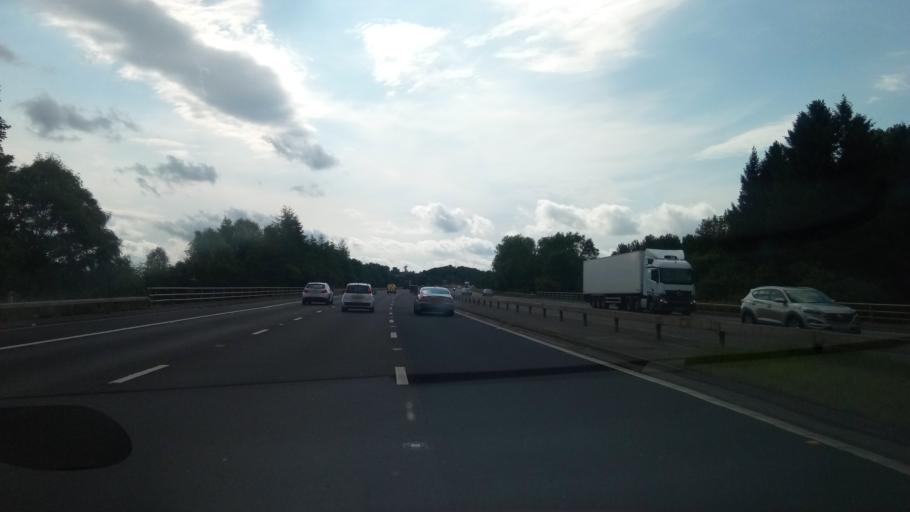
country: GB
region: England
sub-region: Cumbria
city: Penrith
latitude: 54.6433
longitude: -2.7378
